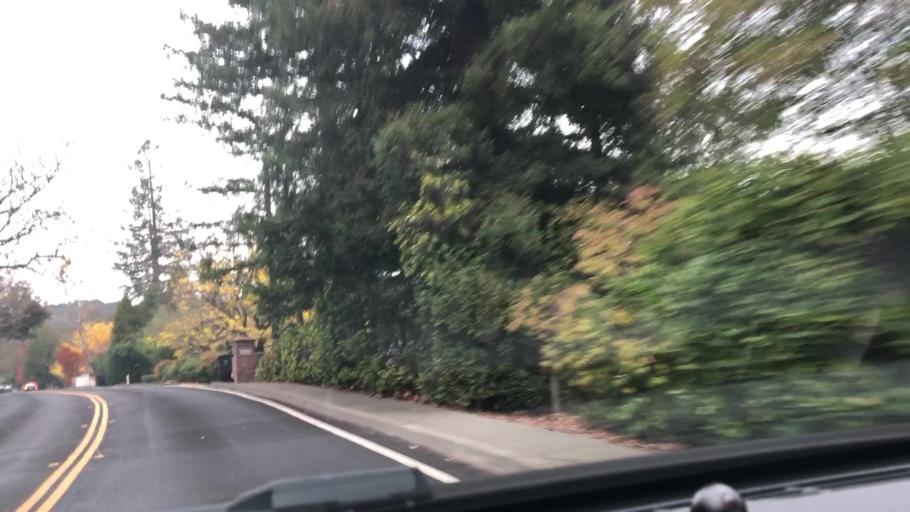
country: US
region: California
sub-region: Contra Costa County
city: Lafayette
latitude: 37.8968
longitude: -122.1509
